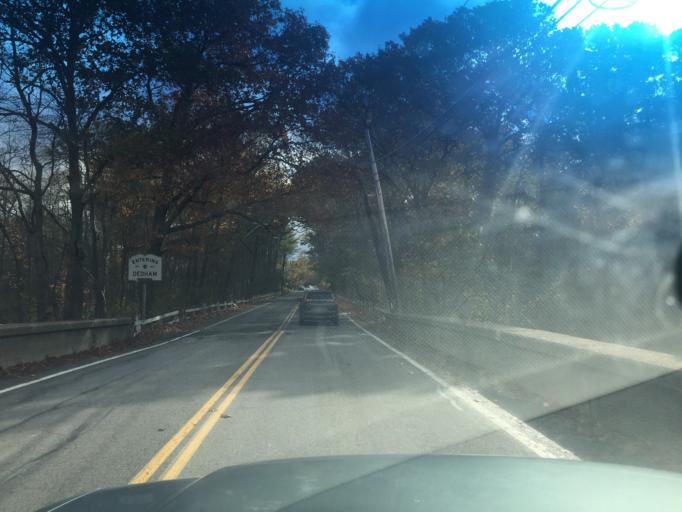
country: US
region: Massachusetts
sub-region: Norfolk County
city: Needham
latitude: 42.2677
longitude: -71.2182
